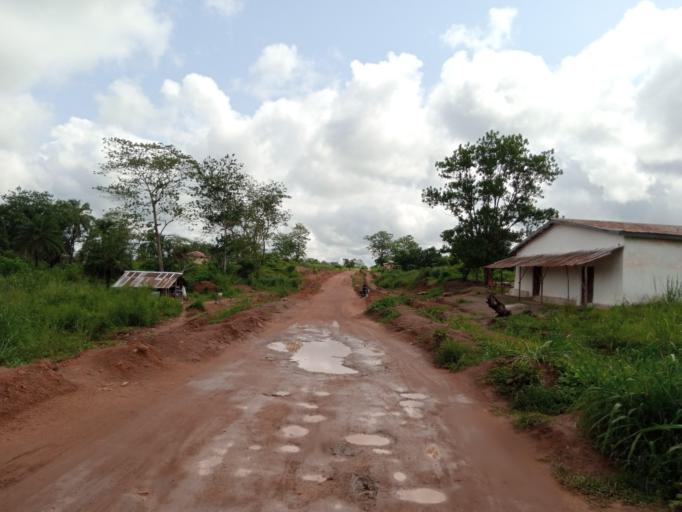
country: SL
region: Southern Province
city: Baoma
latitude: 7.9880
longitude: -11.7369
